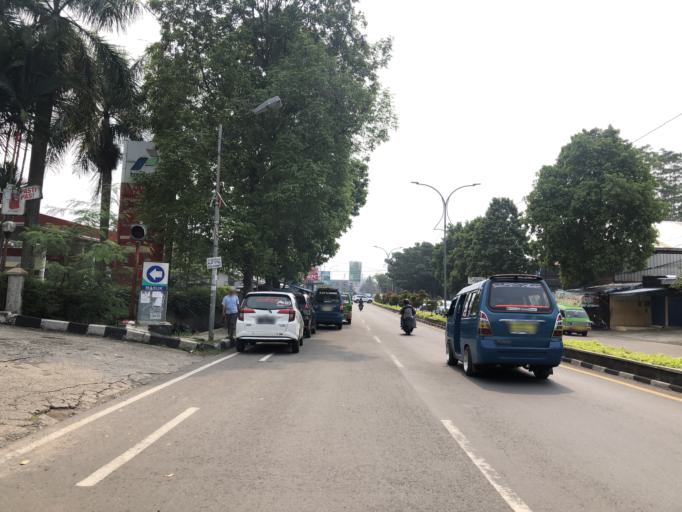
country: ID
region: West Java
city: Bogor
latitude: -6.5722
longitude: 106.7536
